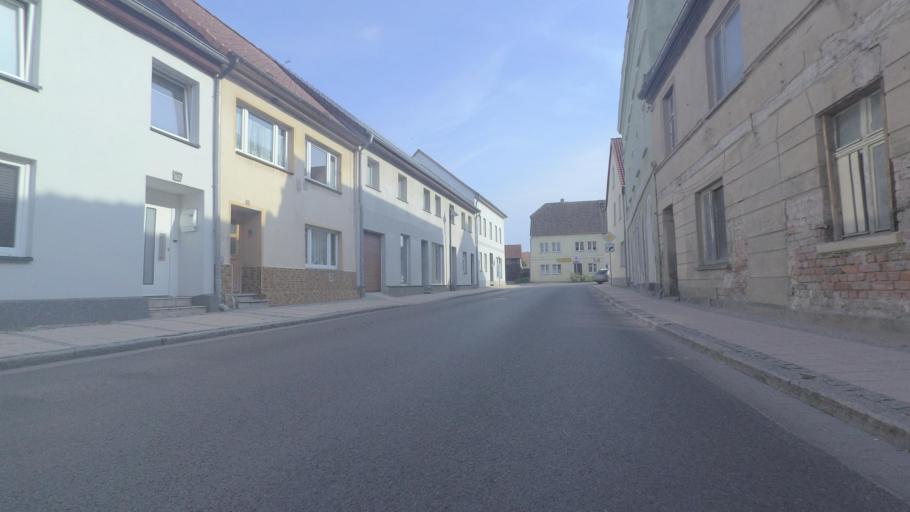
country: DE
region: Mecklenburg-Vorpommern
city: Demmin
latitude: 53.9714
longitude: 13.1296
